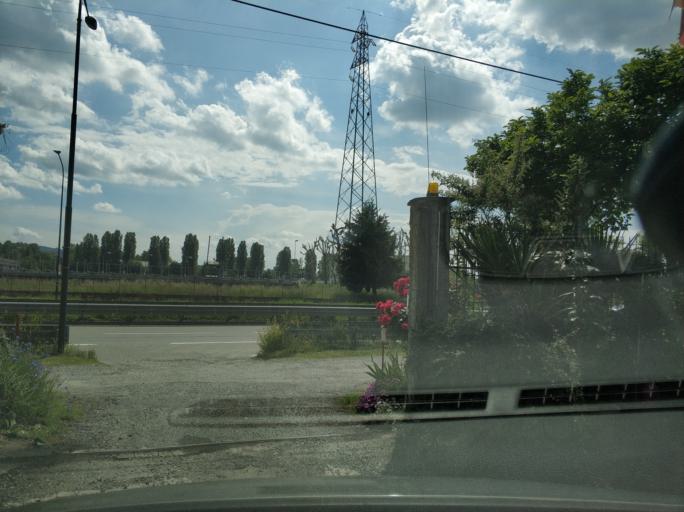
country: IT
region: Piedmont
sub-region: Provincia di Torino
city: San Mauro Torinese
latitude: 45.0953
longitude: 7.7300
